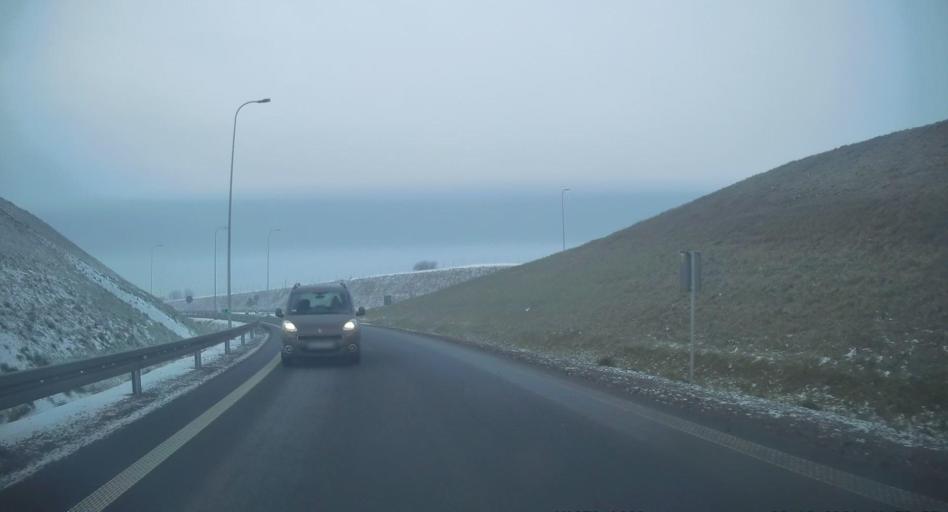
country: PL
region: Lesser Poland Voivodeship
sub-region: Powiat miechowski
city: Miechow
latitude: 50.3125
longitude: 20.0367
